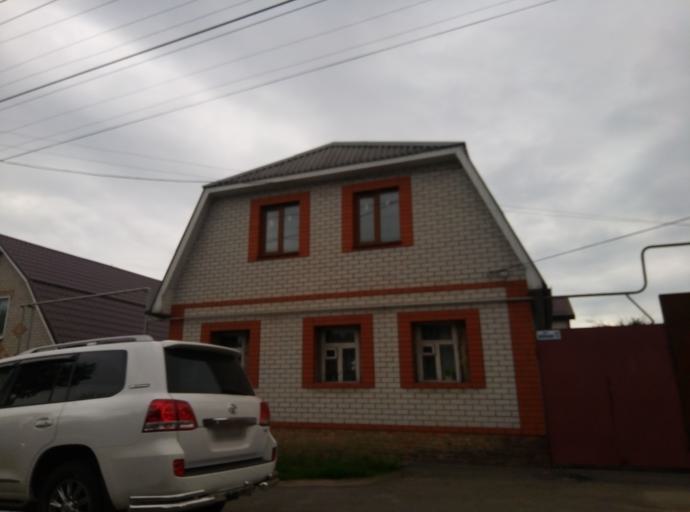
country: RU
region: Kursk
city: Kursk
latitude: 51.7439
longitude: 36.1588
